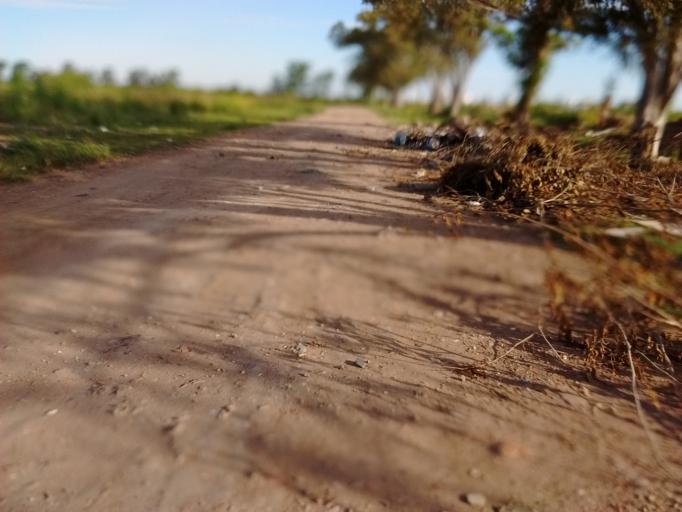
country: AR
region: Santa Fe
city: Funes
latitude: -32.8977
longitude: -60.7964
